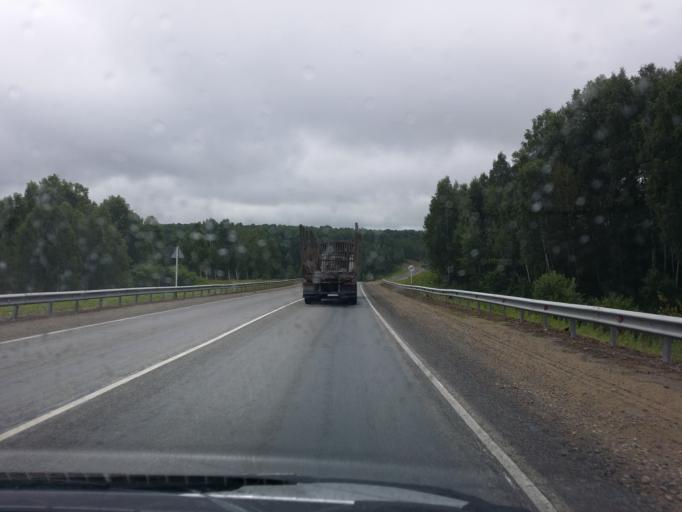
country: RU
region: Altai Krai
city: Nalobikha
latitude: 53.1492
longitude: 84.7051
